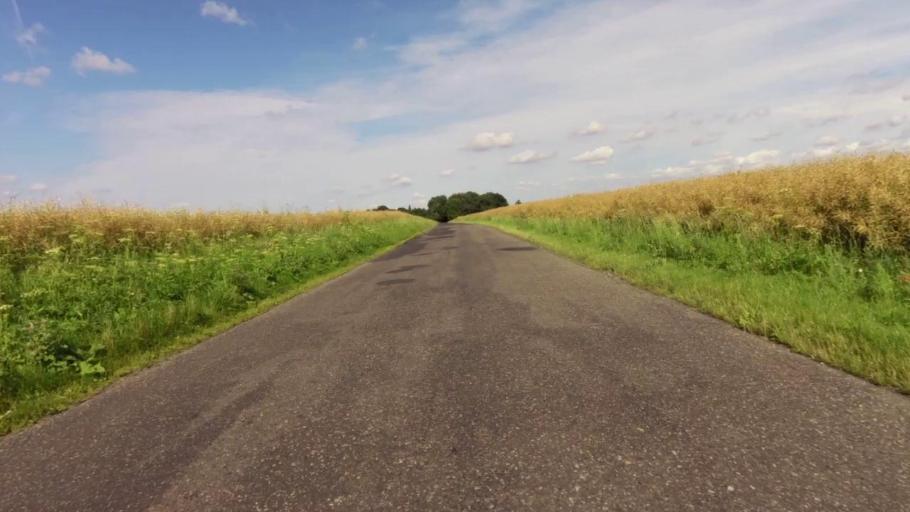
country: PL
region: West Pomeranian Voivodeship
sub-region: Powiat stargardzki
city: Stara Dabrowa
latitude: 53.3456
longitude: 15.1543
